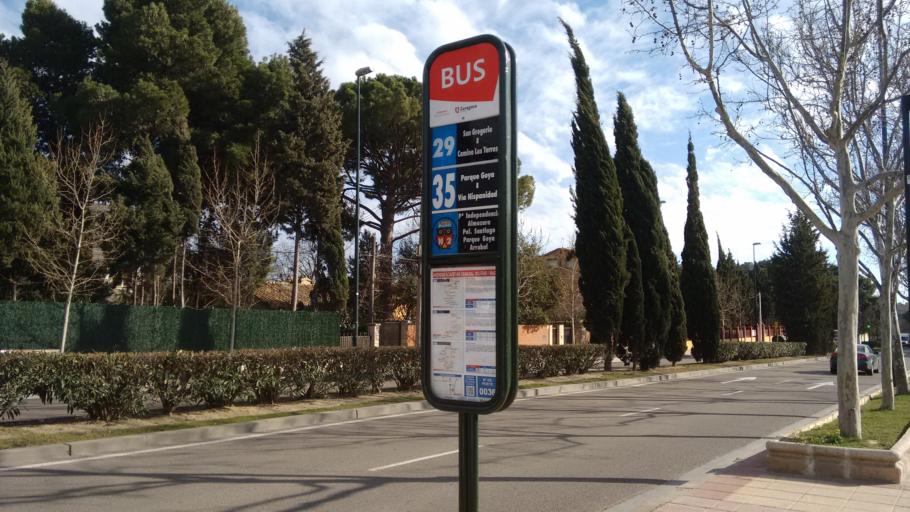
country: ES
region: Aragon
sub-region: Provincia de Zaragoza
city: Zaragoza
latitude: 41.6849
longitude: -0.8710
